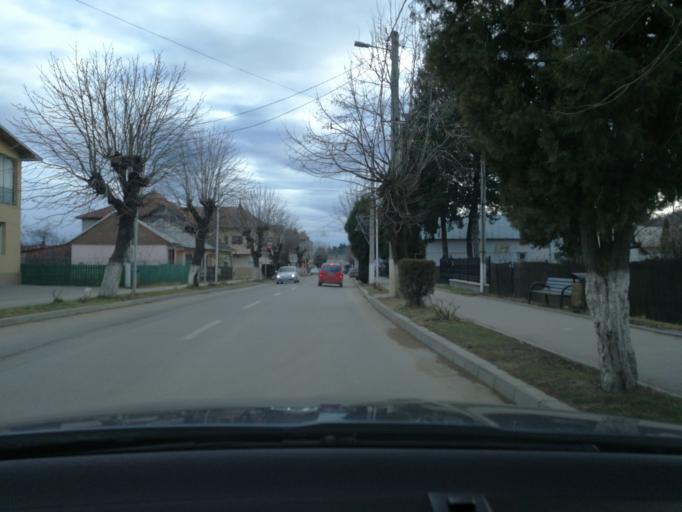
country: RO
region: Prahova
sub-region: Oras Breaza
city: Breaza
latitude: 45.1787
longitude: 25.6698
